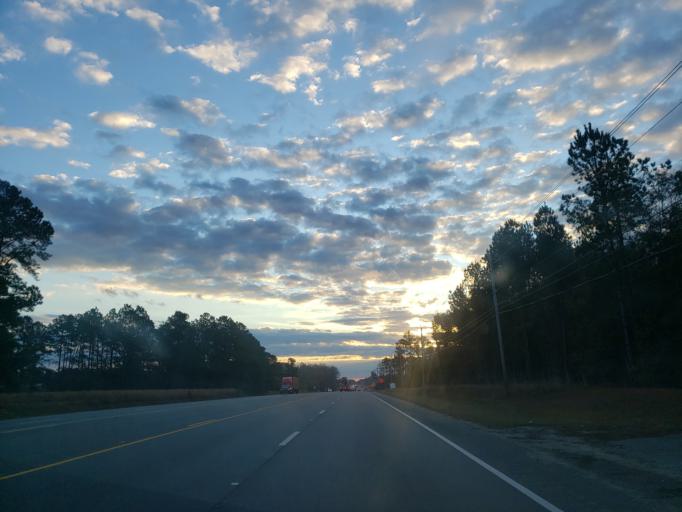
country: US
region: Georgia
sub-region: Chatham County
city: Bloomingdale
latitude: 32.1399
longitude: -81.3226
